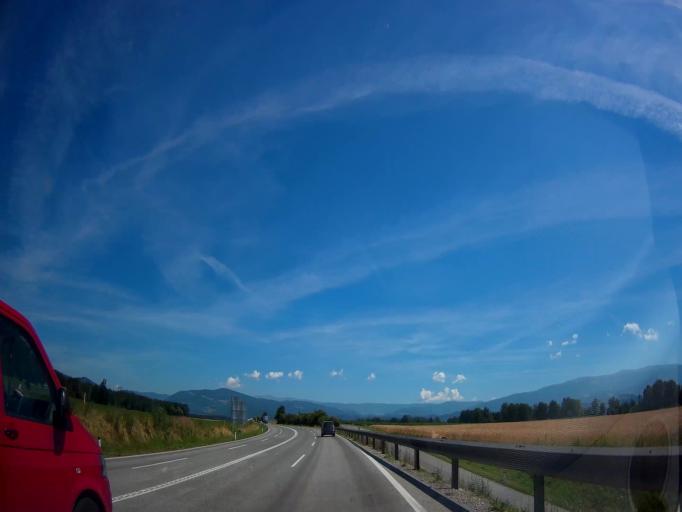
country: AT
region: Carinthia
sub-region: Politischer Bezirk Sankt Veit an der Glan
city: Molbling
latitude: 46.8217
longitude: 14.4373
